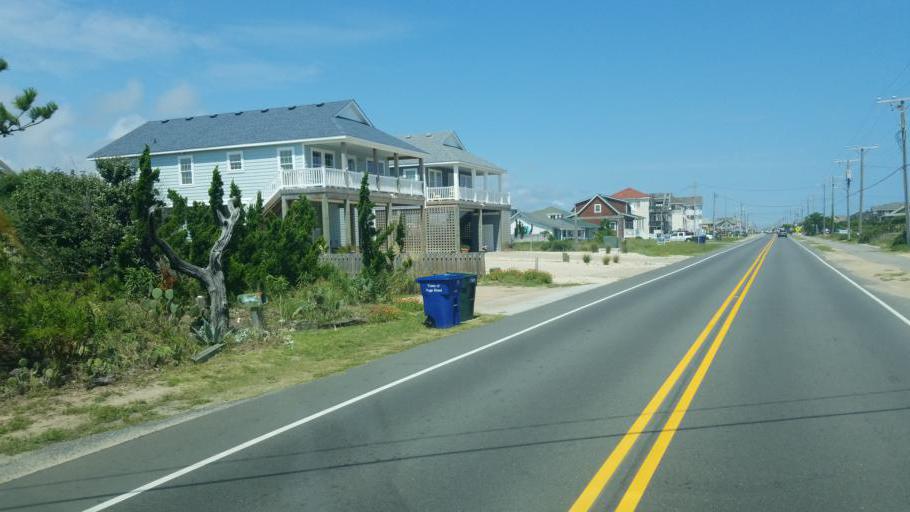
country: US
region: North Carolina
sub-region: Dare County
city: Nags Head
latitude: 35.9760
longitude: -75.6347
